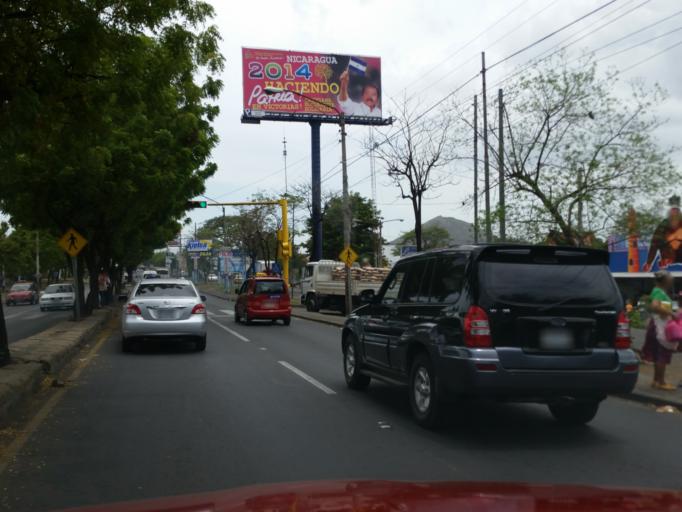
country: NI
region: Managua
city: Ciudad Sandino
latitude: 12.1243
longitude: -86.3044
